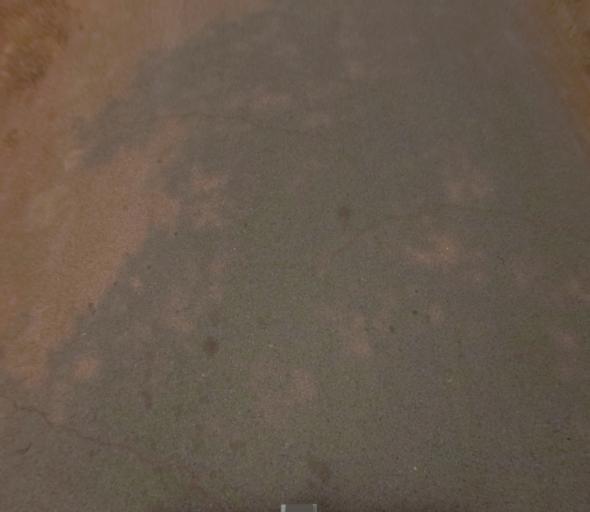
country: US
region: California
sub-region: Madera County
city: Oakhurst
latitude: 37.3284
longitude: -119.6435
